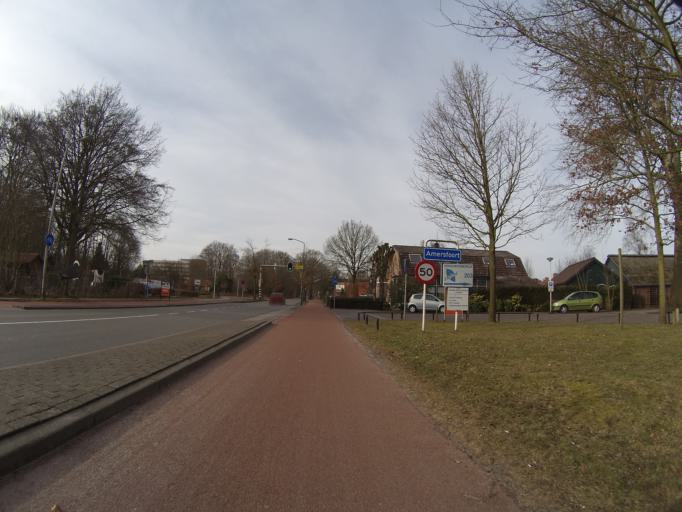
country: NL
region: Utrecht
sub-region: Gemeente Amersfoort
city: Randenbroek
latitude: 52.1443
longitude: 5.4058
